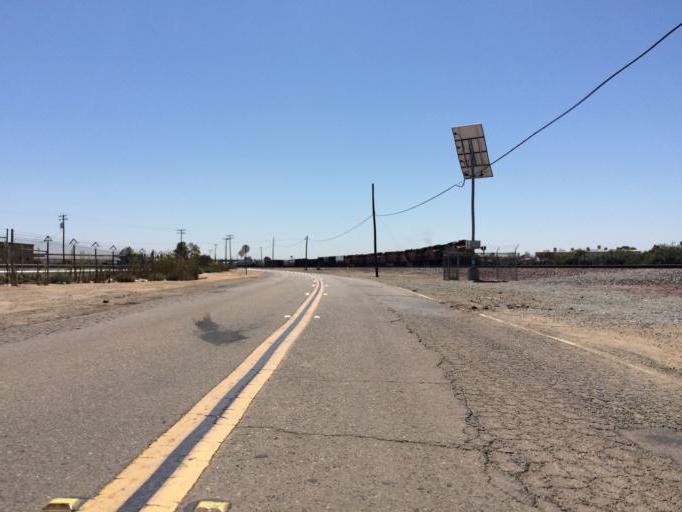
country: US
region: California
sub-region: Fresno County
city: Fresno
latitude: 36.7136
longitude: -119.7718
